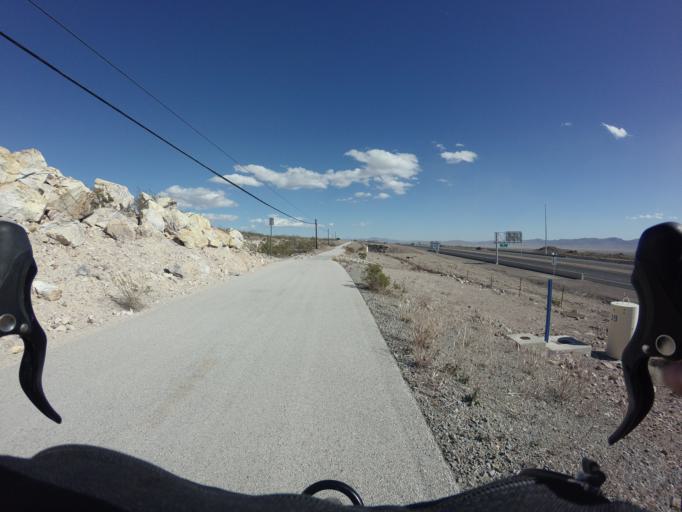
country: US
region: Nevada
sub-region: Clark County
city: Boulder City
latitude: 35.9686
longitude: -114.9029
